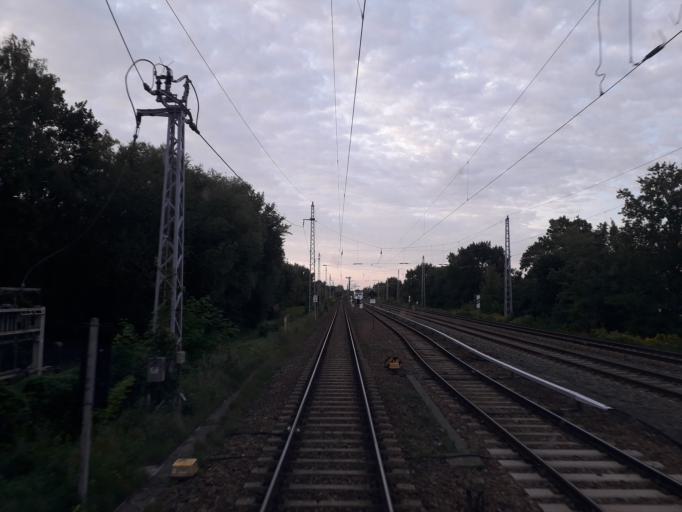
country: DE
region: Brandenburg
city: Hennigsdorf
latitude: 52.6508
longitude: 13.2035
